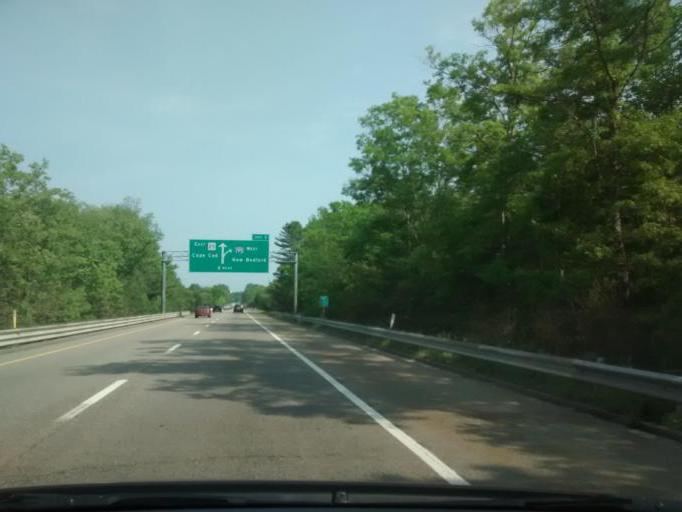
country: US
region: Massachusetts
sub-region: Plymouth County
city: West Wareham
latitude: 41.8038
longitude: -70.7660
